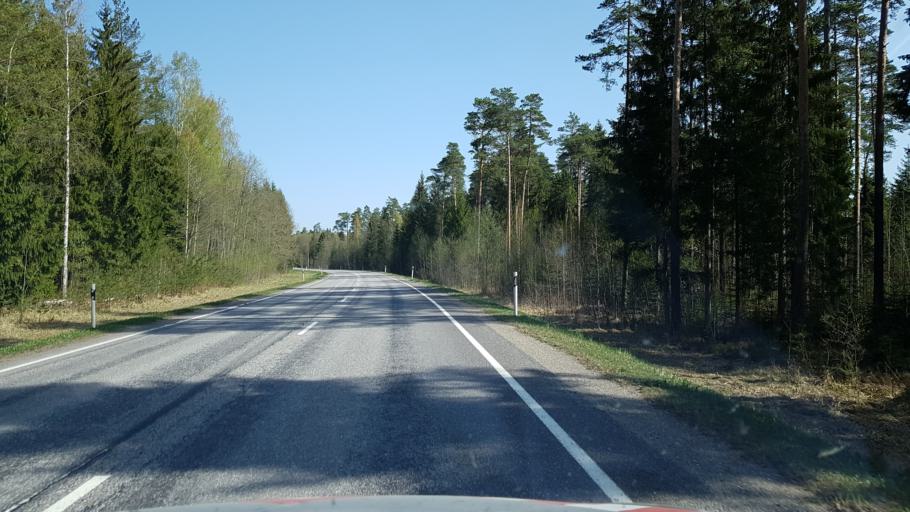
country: EE
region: Viljandimaa
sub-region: Moisakuela linn
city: Moisakula
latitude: 58.2304
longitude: 25.1154
